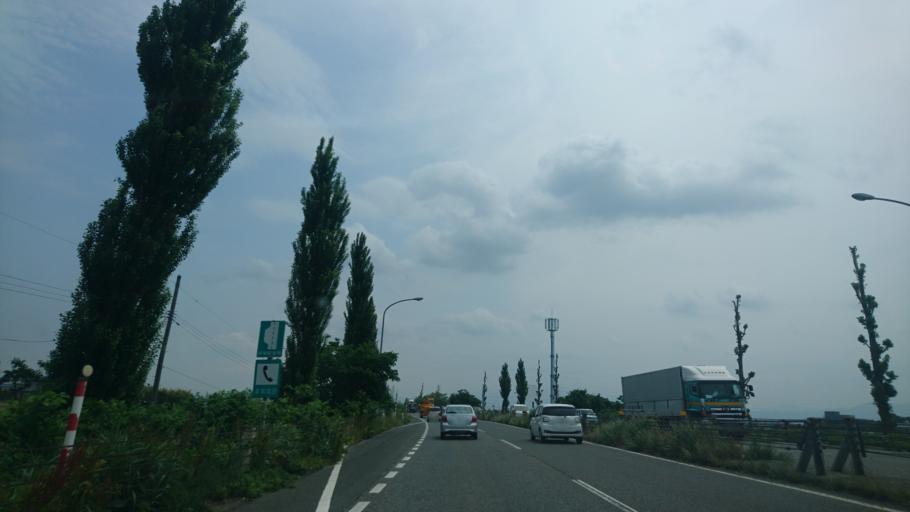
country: JP
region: Niigata
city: Kameda-honcho
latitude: 37.9354
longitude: 139.1650
